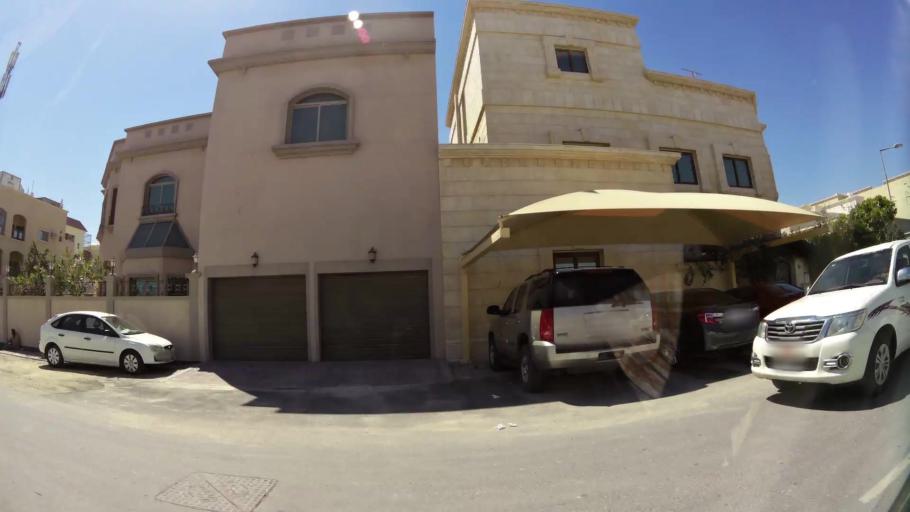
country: BH
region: Muharraq
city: Al Muharraq
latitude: 26.2701
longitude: 50.6009
